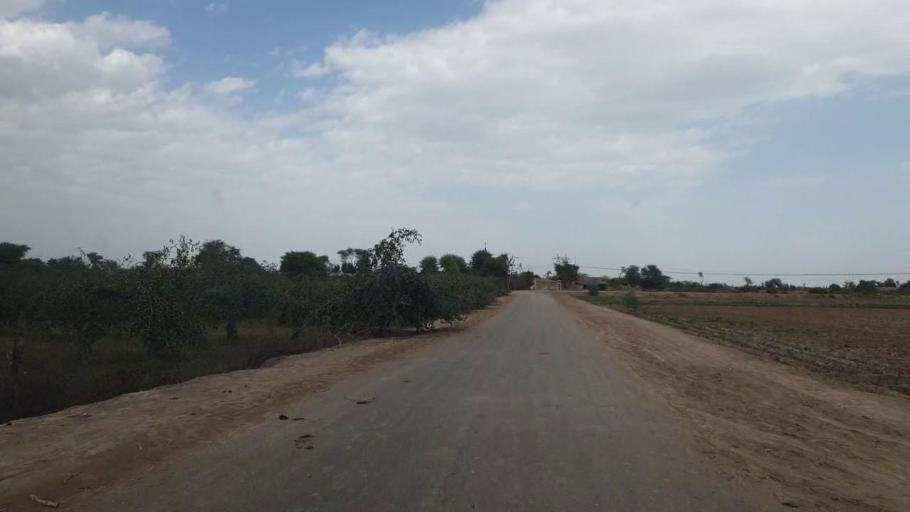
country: PK
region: Sindh
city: Hala
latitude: 25.9779
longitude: 68.4058
